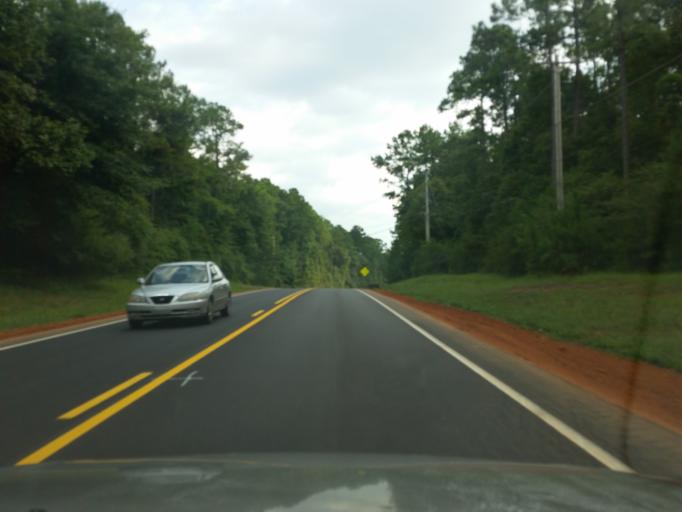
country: US
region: Alabama
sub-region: Baldwin County
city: Spanish Fort
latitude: 30.7091
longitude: -87.9012
